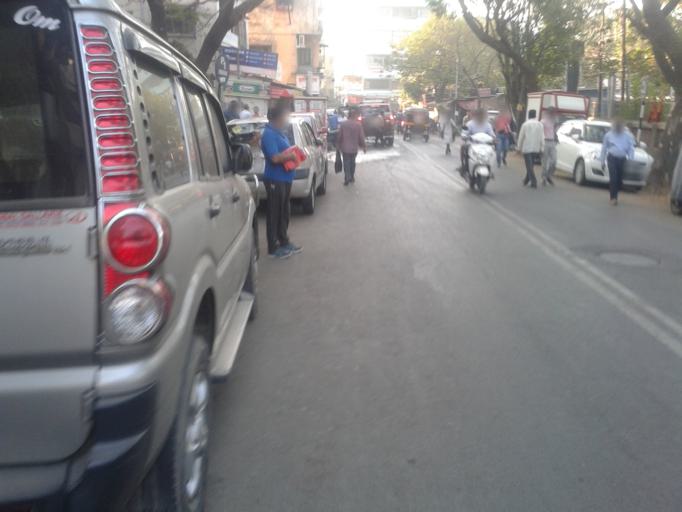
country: IN
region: Maharashtra
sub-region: Thane
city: Dombivli
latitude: 19.2127
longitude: 73.0893
